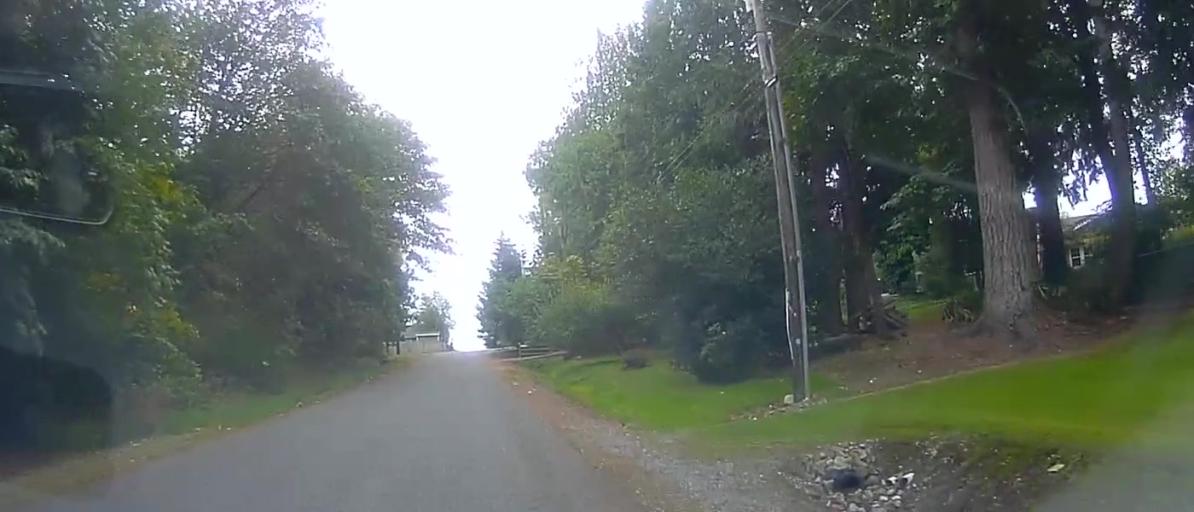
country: US
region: Washington
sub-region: Skagit County
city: Burlington
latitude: 48.4439
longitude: -122.2947
